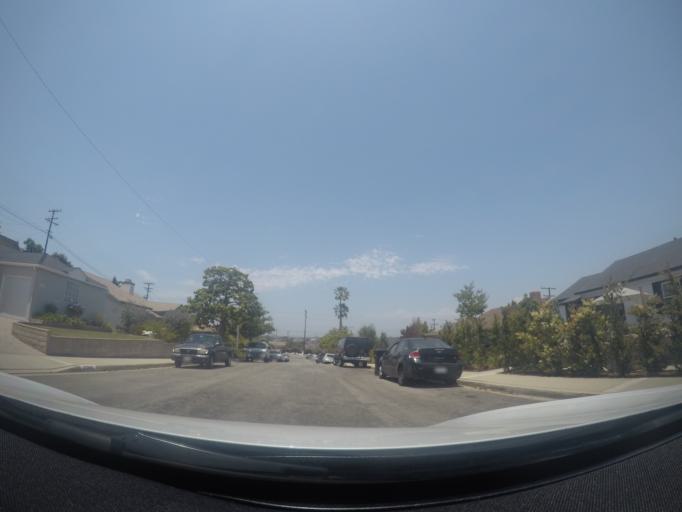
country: US
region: California
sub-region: Los Angeles County
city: Redondo Beach
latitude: 33.8261
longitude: -118.3706
